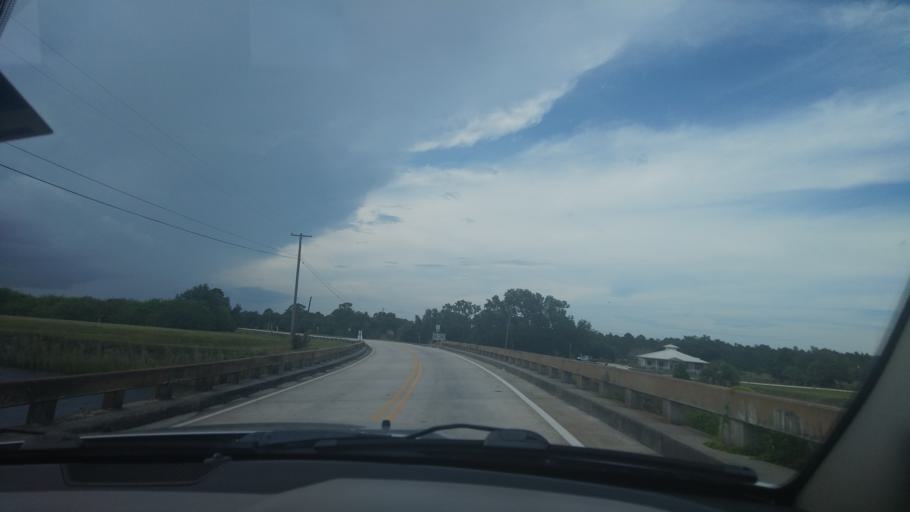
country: US
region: Florida
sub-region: Indian River County
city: Fellsmere
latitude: 27.8232
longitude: -80.6071
